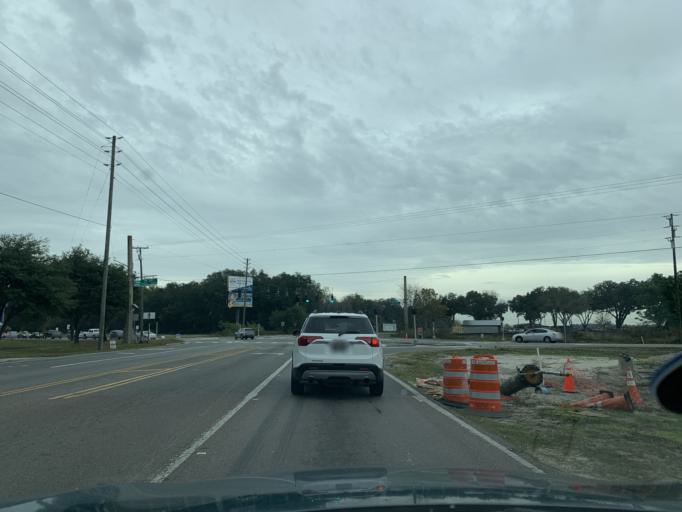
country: US
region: Florida
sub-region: Pasco County
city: Zephyrhills South
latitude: 28.2081
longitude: -82.1859
